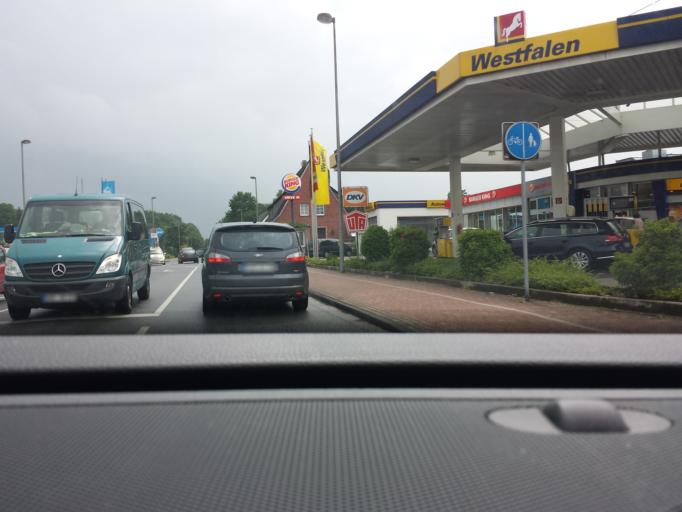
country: DE
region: North Rhine-Westphalia
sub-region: Regierungsbezirk Munster
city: Ahaus
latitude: 52.0738
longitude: 6.9972
